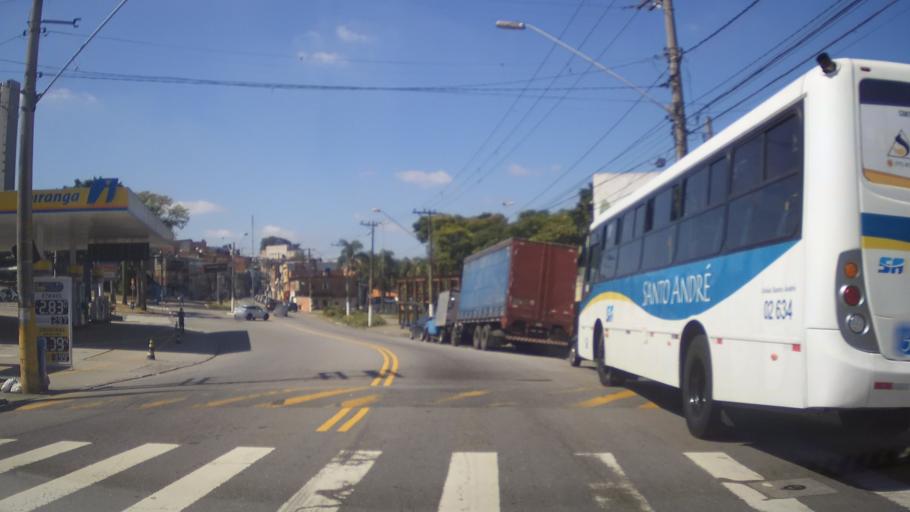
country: BR
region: Sao Paulo
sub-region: Santo Andre
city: Santo Andre
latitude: -23.6483
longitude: -46.5568
